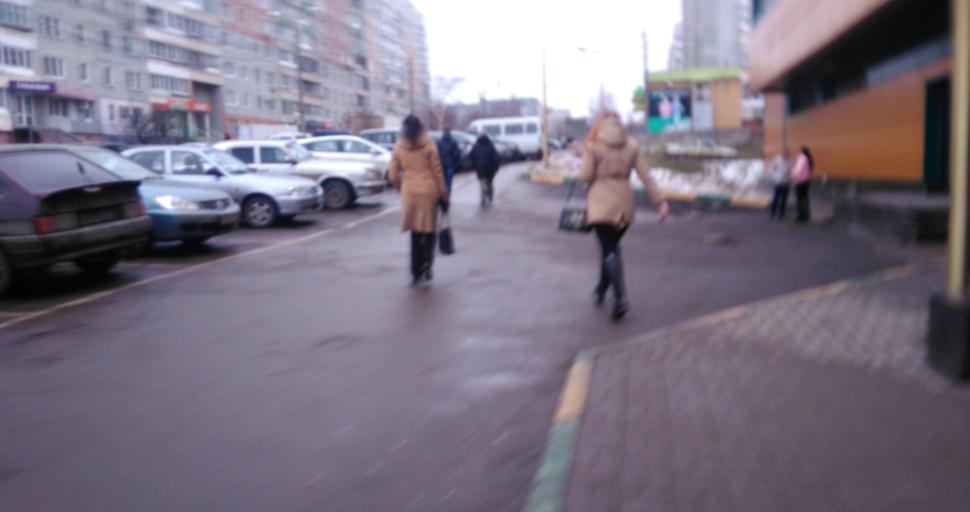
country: RU
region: Tula
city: Tula
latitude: 54.2029
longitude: 37.6328
